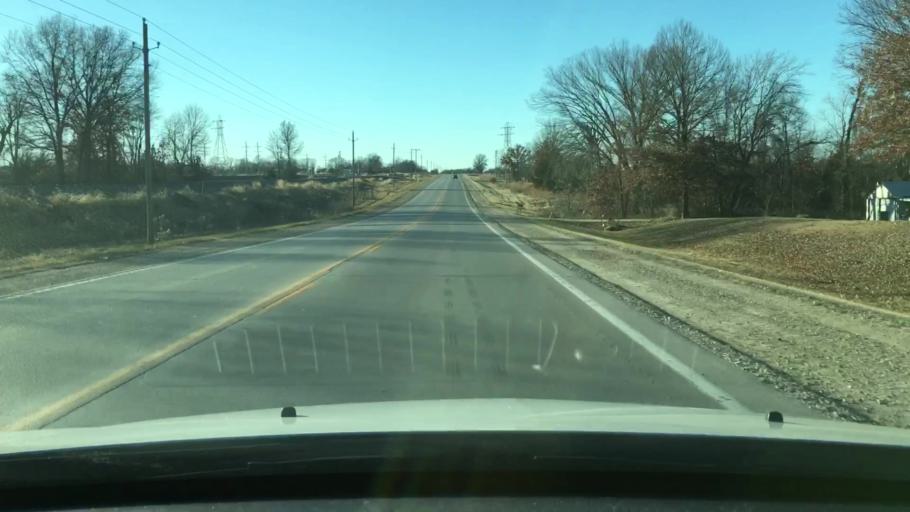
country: US
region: Missouri
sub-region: Audrain County
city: Mexico
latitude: 39.1871
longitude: -91.9535
